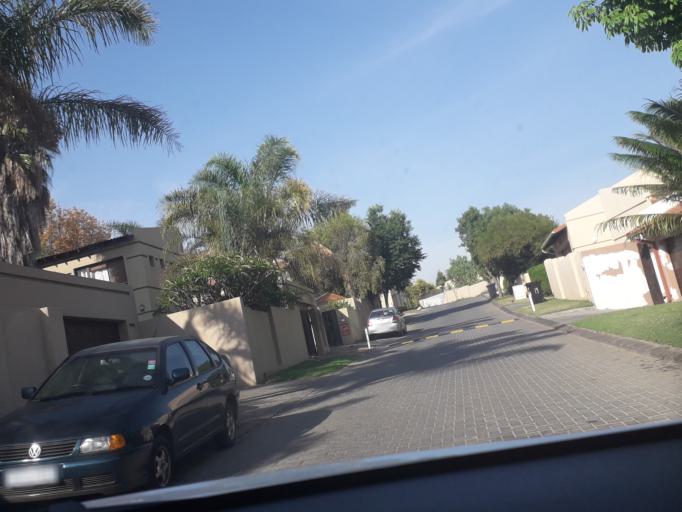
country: ZA
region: Gauteng
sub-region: City of Johannesburg Metropolitan Municipality
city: Diepsloot
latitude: -26.0452
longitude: 27.9820
